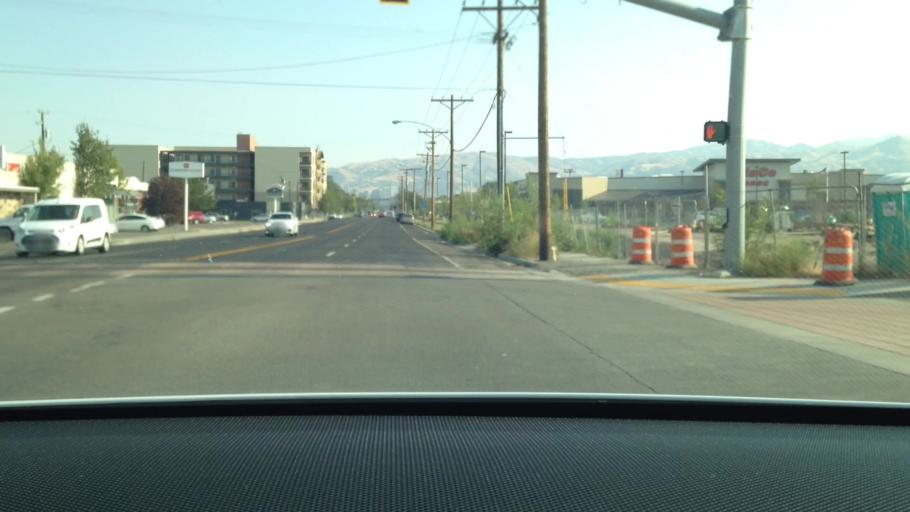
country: US
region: Utah
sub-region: Salt Lake County
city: South Salt Lake
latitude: 40.7222
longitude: -111.8911
